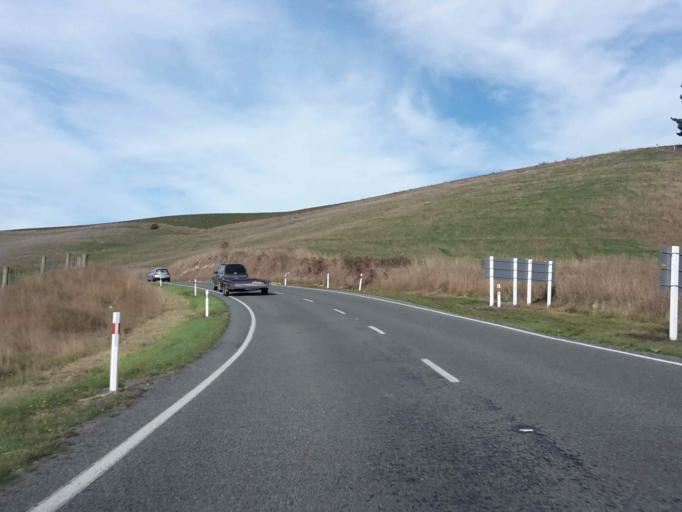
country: NZ
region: Canterbury
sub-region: Timaru District
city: Pleasant Point
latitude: -44.0890
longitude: 170.9592
